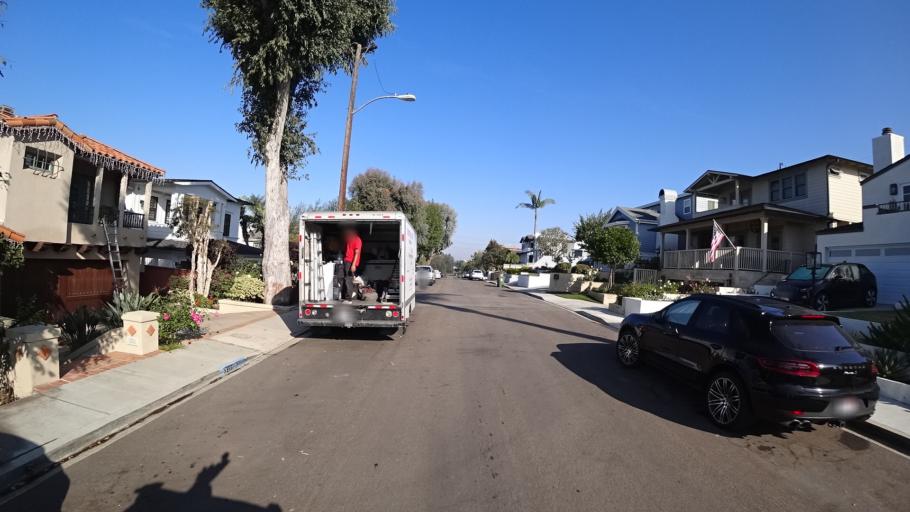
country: US
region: California
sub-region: Los Angeles County
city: Manhattan Beach
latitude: 33.8990
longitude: -118.4017
